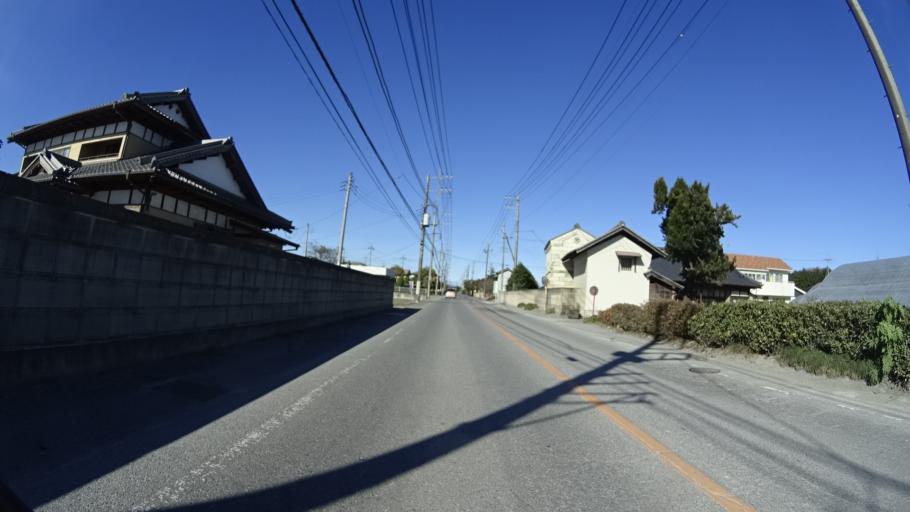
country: JP
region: Tochigi
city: Mibu
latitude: 36.4584
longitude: 139.7536
